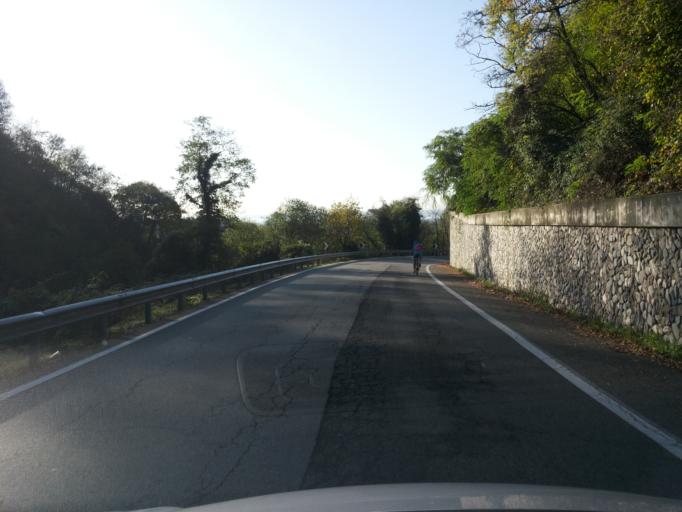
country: IT
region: Piedmont
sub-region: Provincia di Torino
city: Villareggia
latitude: 45.3034
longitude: 7.9668
